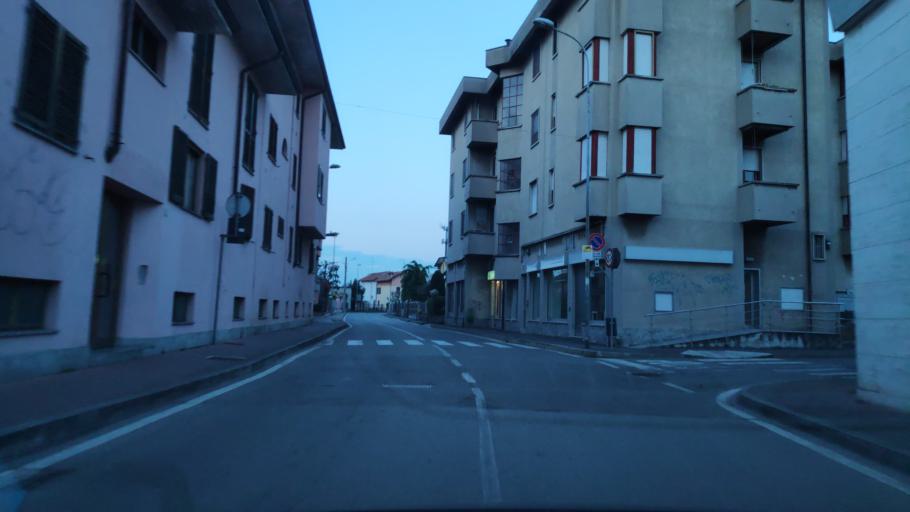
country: IT
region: Lombardy
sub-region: Citta metropolitana di Milano
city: Liscate
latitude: 45.4806
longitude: 9.4097
